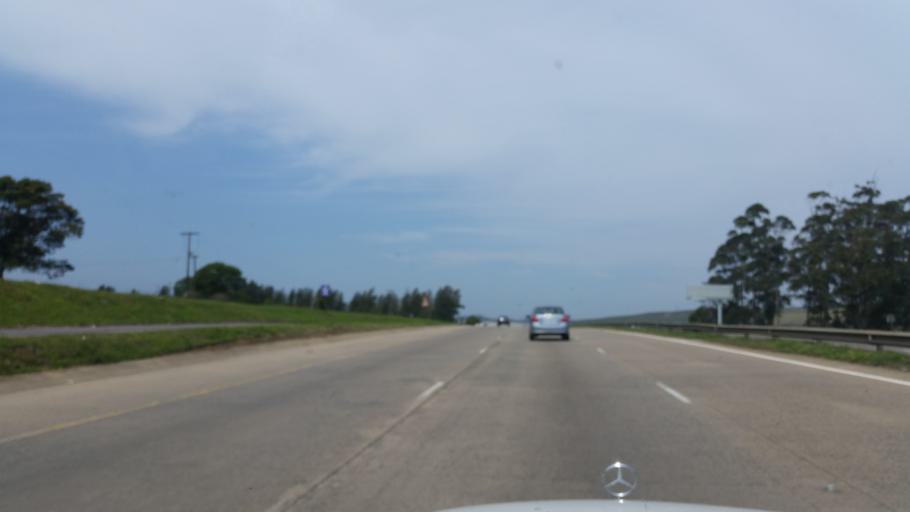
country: ZA
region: KwaZulu-Natal
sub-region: uMgungundlovu District Municipality
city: Camperdown
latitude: -29.7373
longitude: 30.6065
